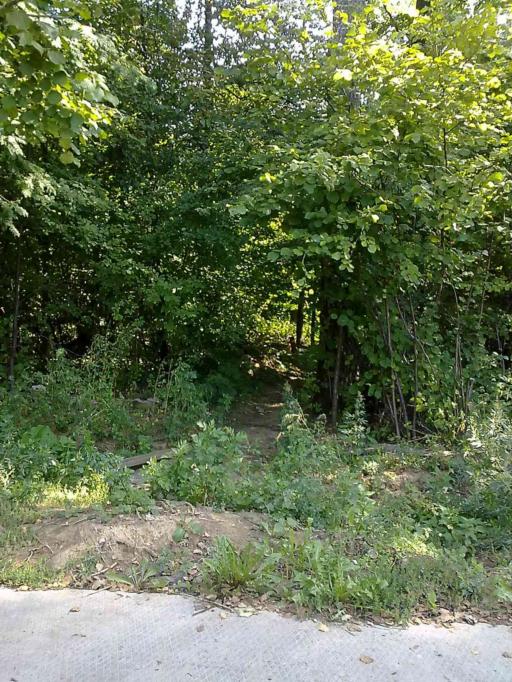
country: RU
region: Moskovskaya
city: Kommunarka
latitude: 55.5736
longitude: 37.5186
